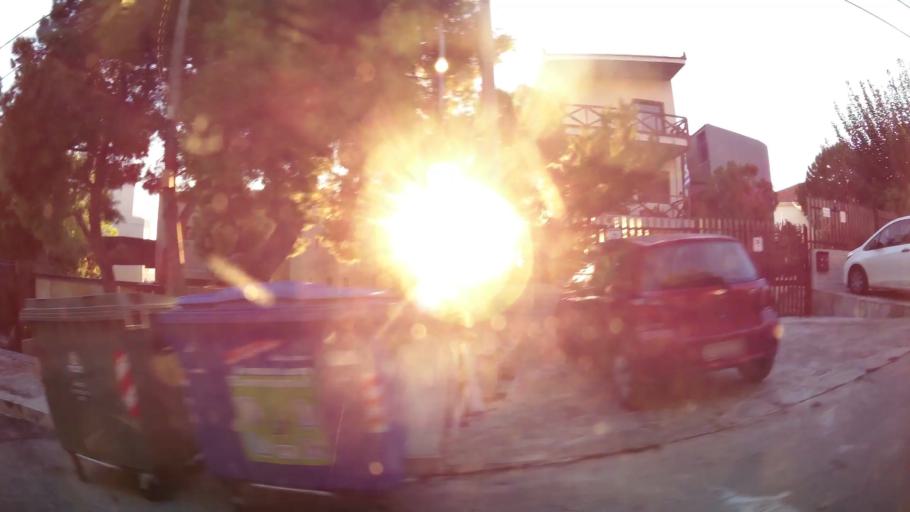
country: GR
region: Attica
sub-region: Nomarchia Athinas
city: Penteli
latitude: 38.0477
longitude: 23.8566
